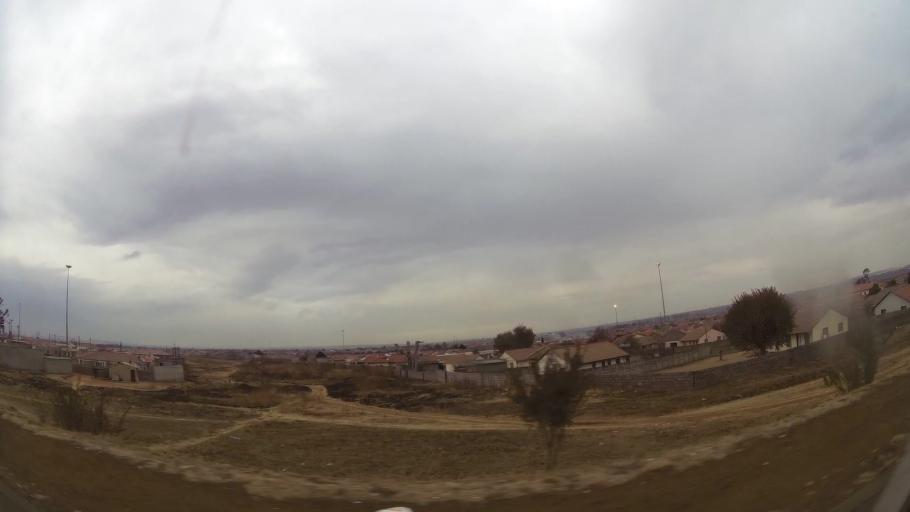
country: ZA
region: Gauteng
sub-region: Ekurhuleni Metropolitan Municipality
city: Germiston
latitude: -26.3878
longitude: 28.1545
